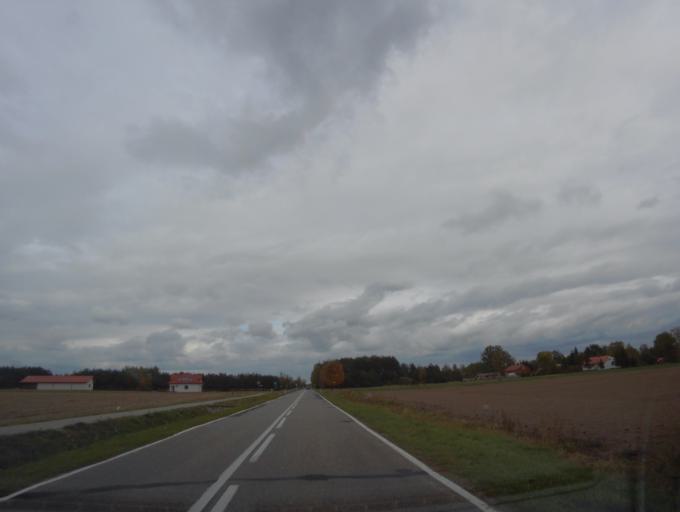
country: PL
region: Lublin Voivodeship
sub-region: Powiat bialski
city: Slawatycze
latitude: 51.7465
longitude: 23.5339
